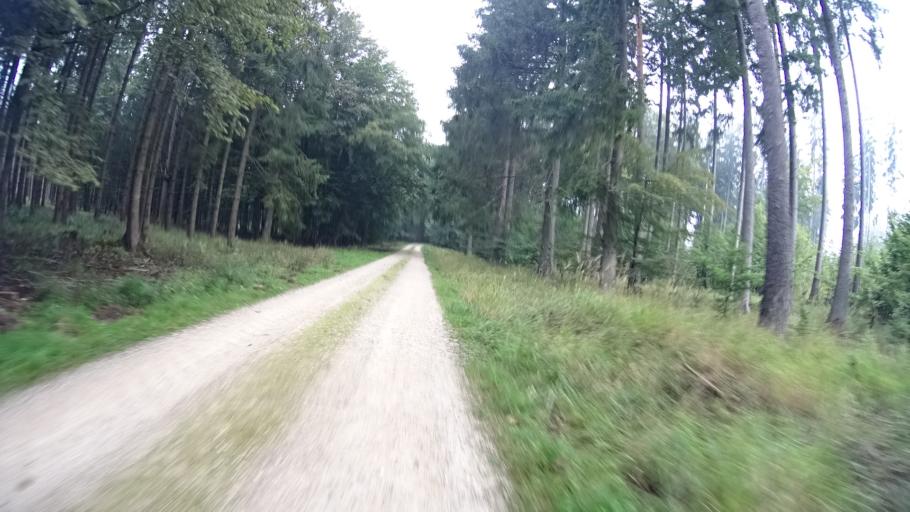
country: DE
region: Bavaria
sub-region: Upper Bavaria
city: Stammham
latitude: 48.8819
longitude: 11.5103
